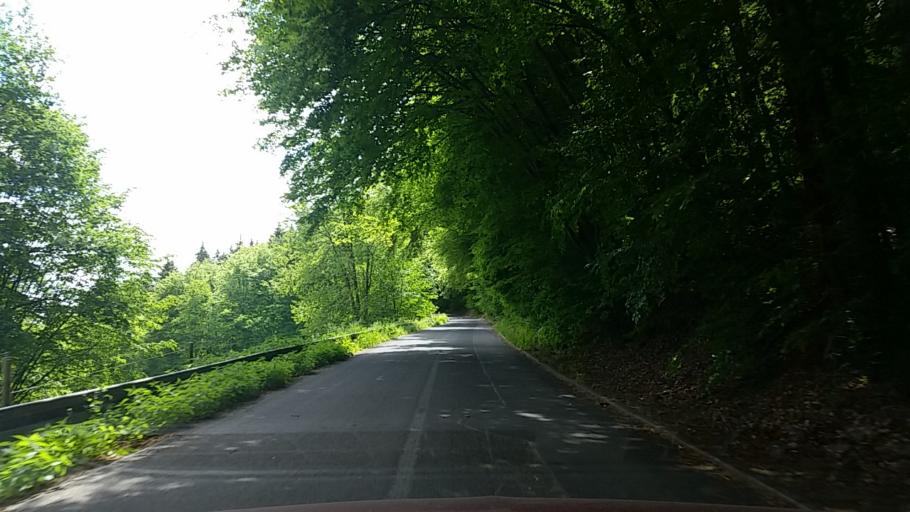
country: DE
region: Bavaria
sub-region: Regierungsbezirk Unterfranken
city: Neuendorf
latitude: 50.0151
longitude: 9.6615
